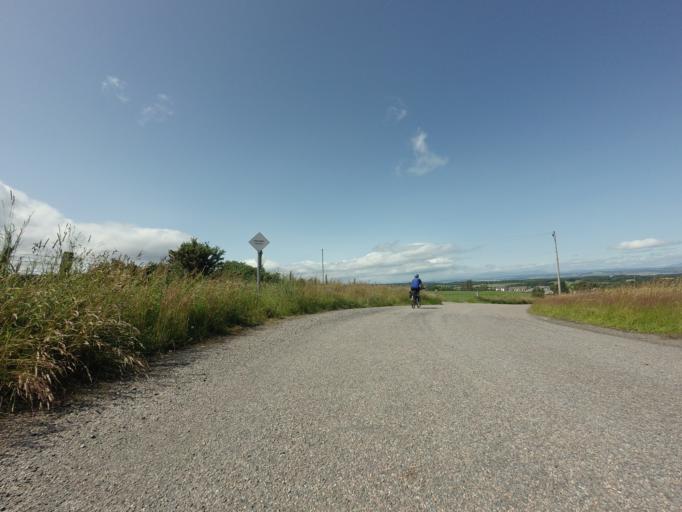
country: GB
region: Scotland
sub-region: Highland
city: Nairn
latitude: 57.5005
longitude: -3.9779
